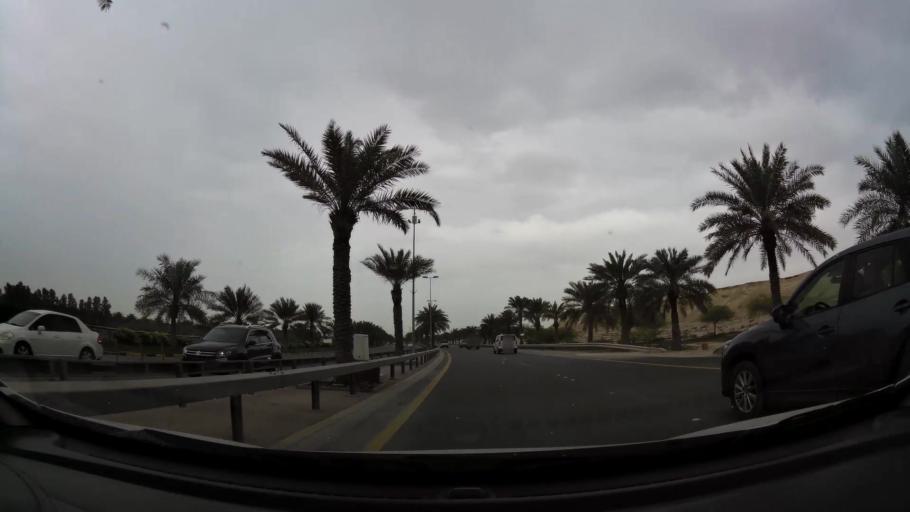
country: BH
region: Northern
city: Ar Rifa'
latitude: 26.1129
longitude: 50.5373
